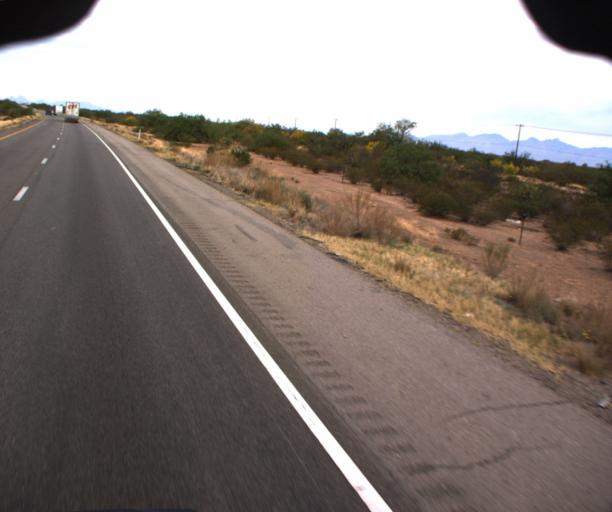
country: US
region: Arizona
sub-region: Pima County
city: Vail
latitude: 32.0429
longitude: -110.7409
